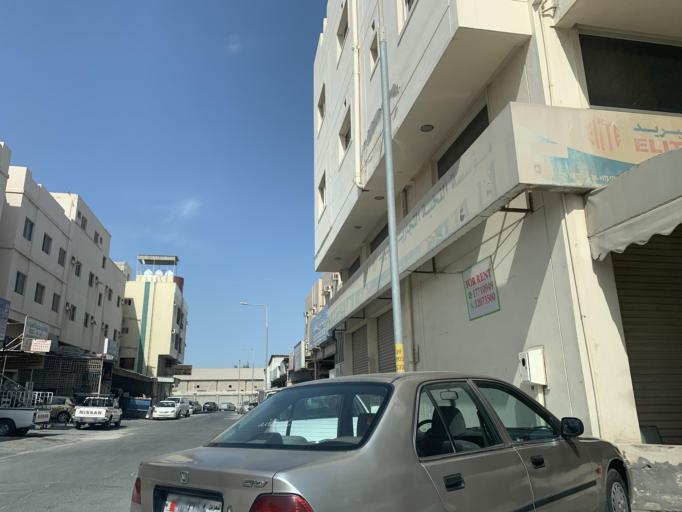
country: BH
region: Northern
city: Ar Rifa'
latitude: 26.1318
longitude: 50.5833
